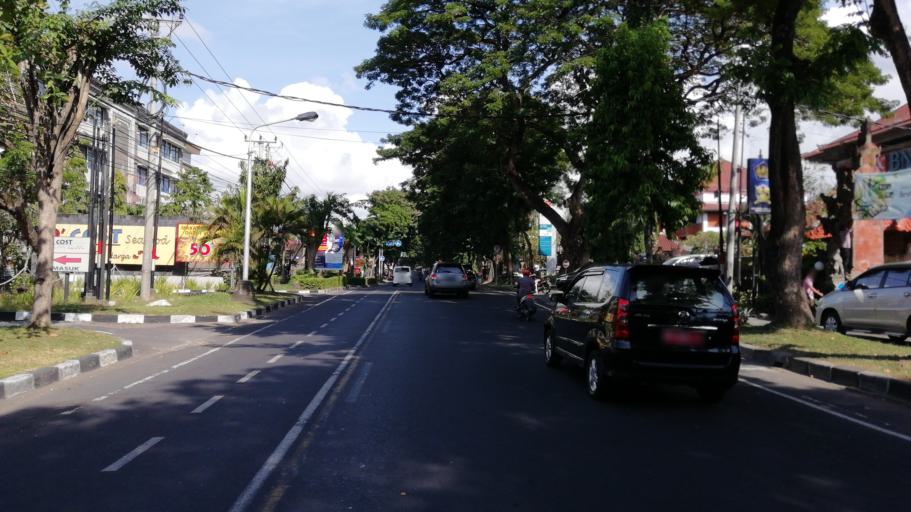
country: ID
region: Bali
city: Denpasar
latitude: -8.6729
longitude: 115.2273
